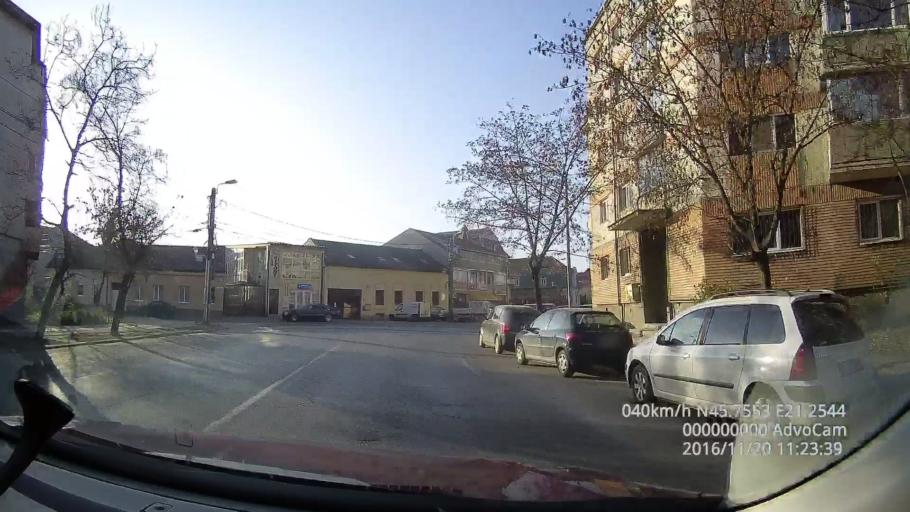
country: RO
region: Timis
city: Timisoara
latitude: 45.7552
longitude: 21.2544
